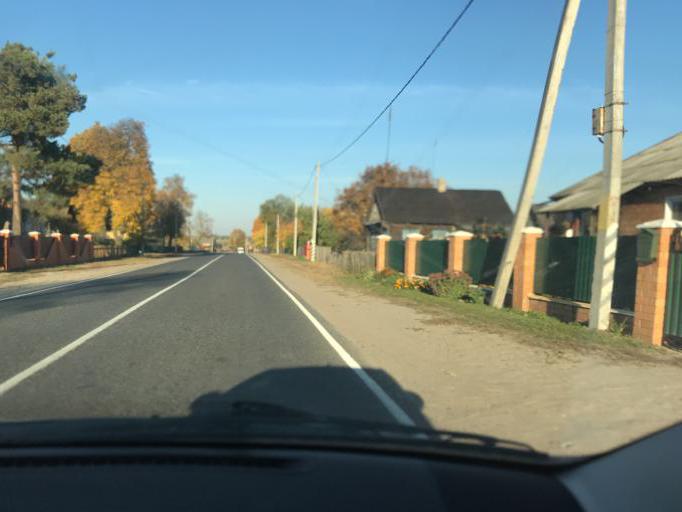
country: BY
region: Brest
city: Stolin
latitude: 51.8347
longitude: 26.7307
